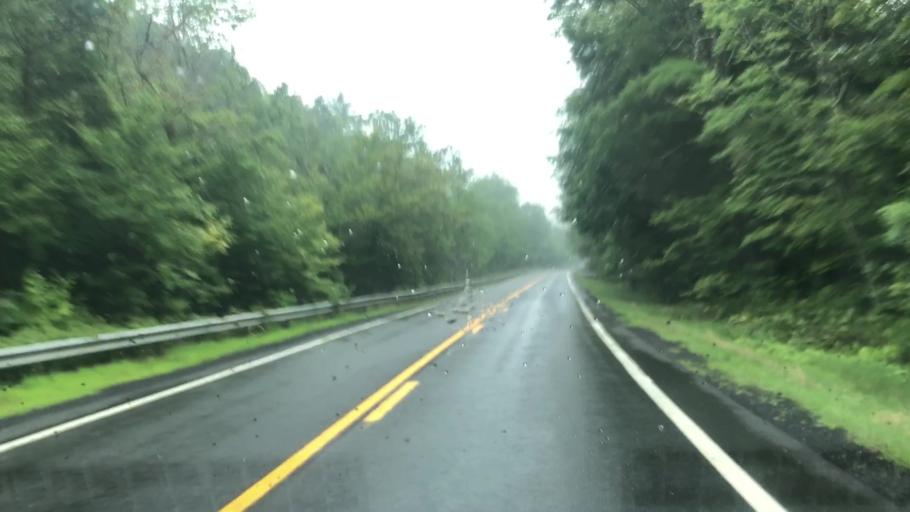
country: US
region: Massachusetts
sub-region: Hampshire County
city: Chesterfield
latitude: 42.3348
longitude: -72.8849
